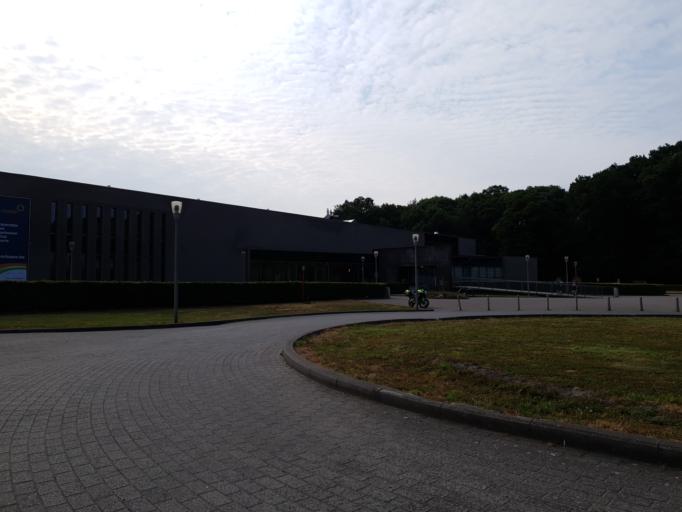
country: BE
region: Flanders
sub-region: Provincie Antwerpen
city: Brasschaat
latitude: 51.2846
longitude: 4.5012
